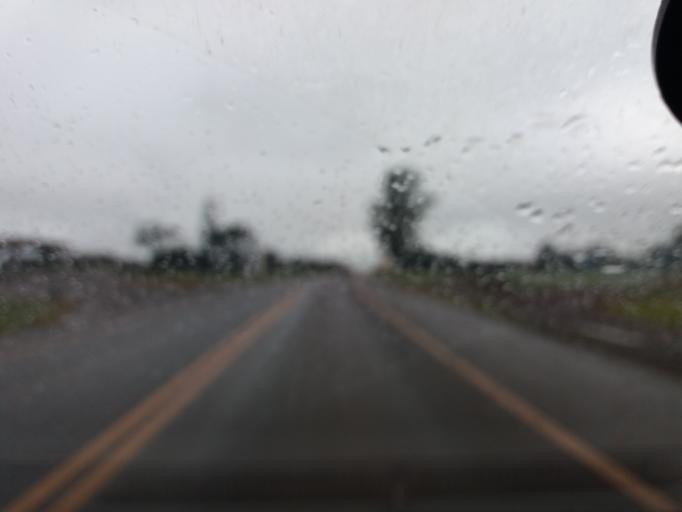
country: BR
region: Parana
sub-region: Moreira Sales
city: Moreira Sales
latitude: -24.3338
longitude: -52.6865
